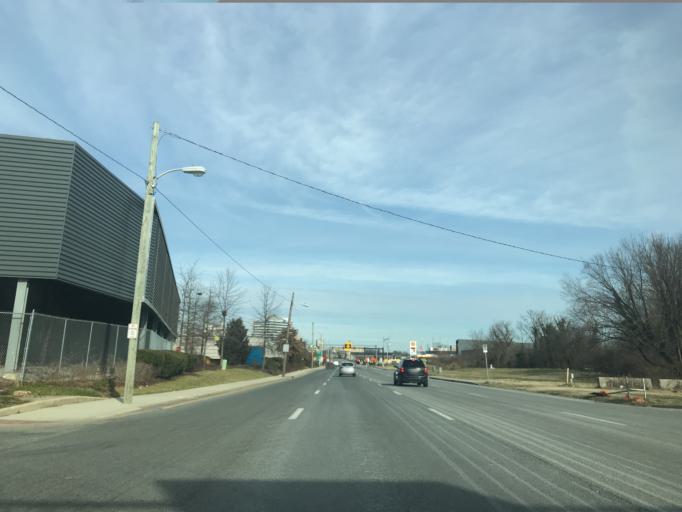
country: US
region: Delaware
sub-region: New Castle County
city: Wilmington
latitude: 39.7306
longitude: -75.5544
